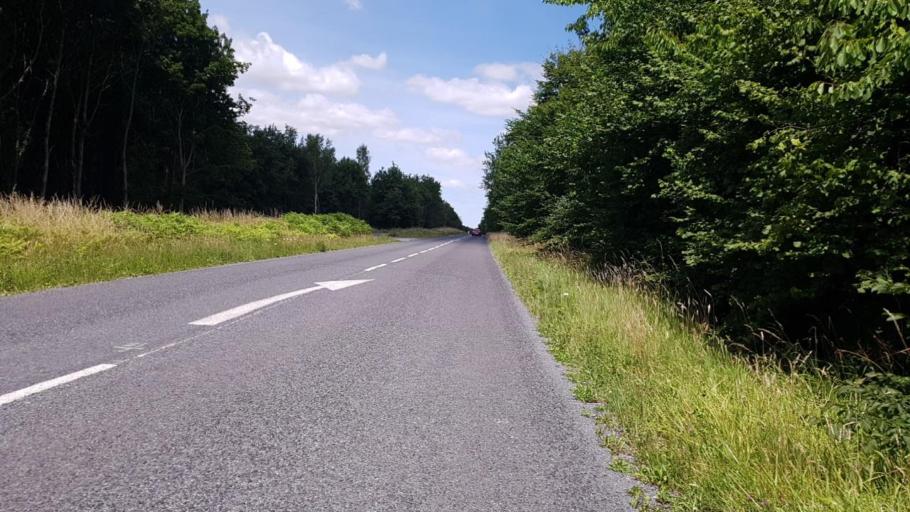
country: FR
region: Picardie
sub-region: Departement de l'Oise
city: Chiry-Ourscamp
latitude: 49.5258
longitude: 2.9839
